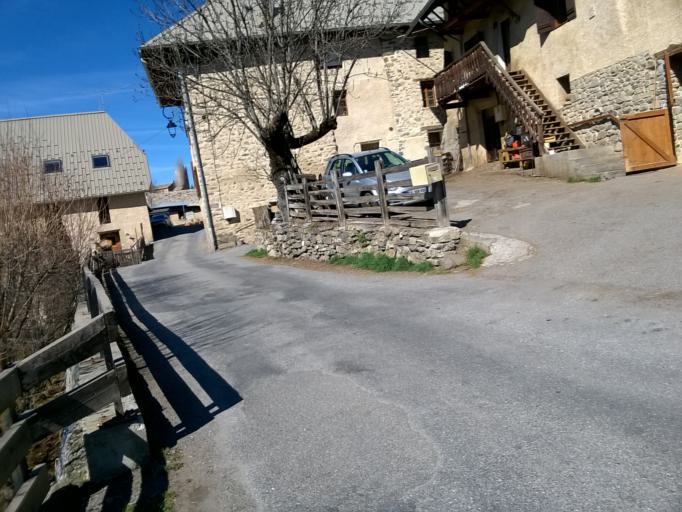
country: FR
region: Provence-Alpes-Cote d'Azur
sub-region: Departement des Hautes-Alpes
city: Embrun
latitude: 44.5132
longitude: 6.5531
